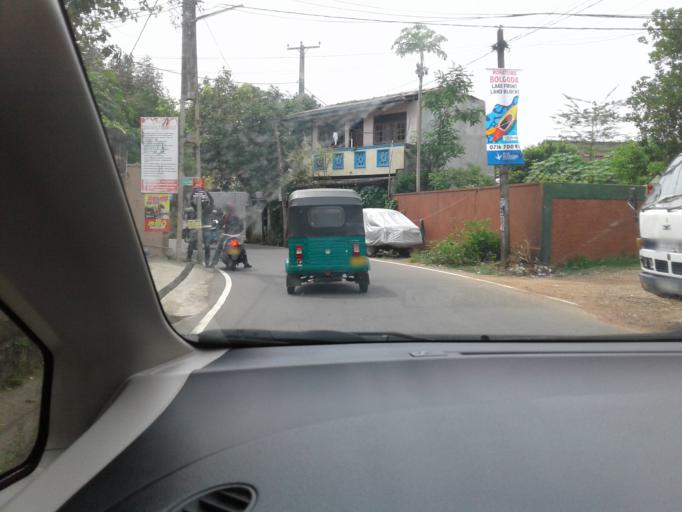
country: LK
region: Western
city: Maharagama
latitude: 6.8502
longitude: 79.9201
